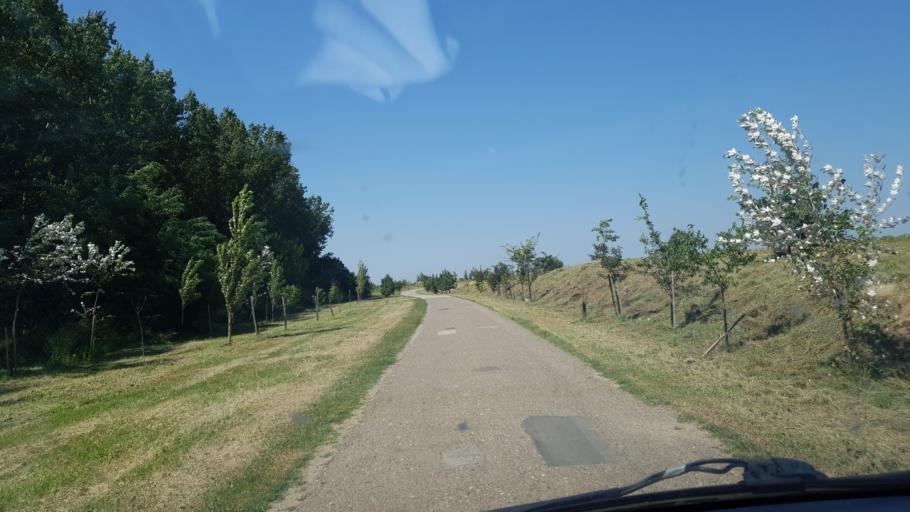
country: RS
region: Autonomna Pokrajina Vojvodina
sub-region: Juznobacki Okrug
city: Kovilj
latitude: 45.2059
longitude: 20.0638
